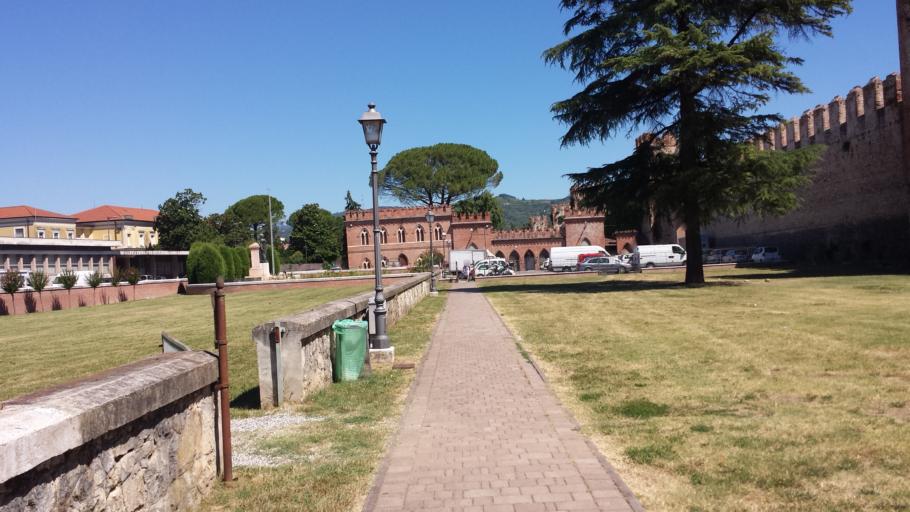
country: IT
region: Veneto
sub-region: Provincia di Verona
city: Soave
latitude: 45.4204
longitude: 11.2461
